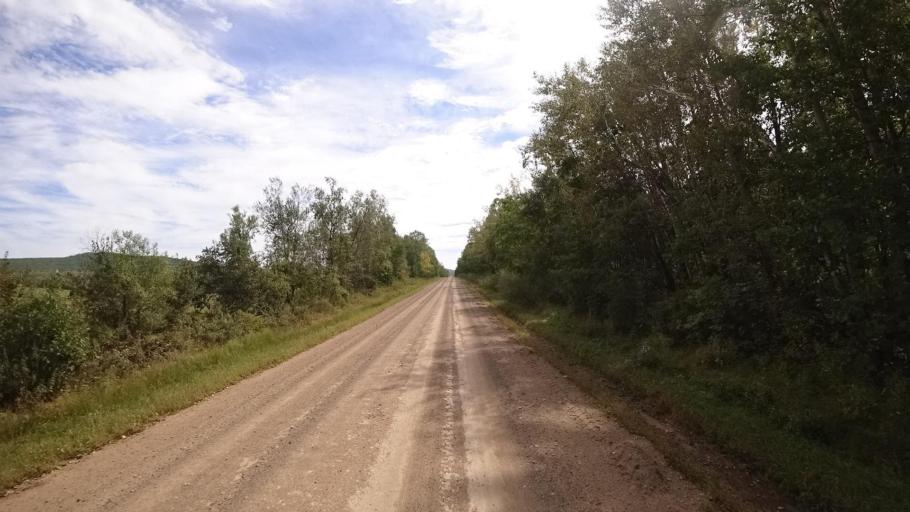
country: RU
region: Primorskiy
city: Yakovlevka
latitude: 44.6113
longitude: 133.5996
